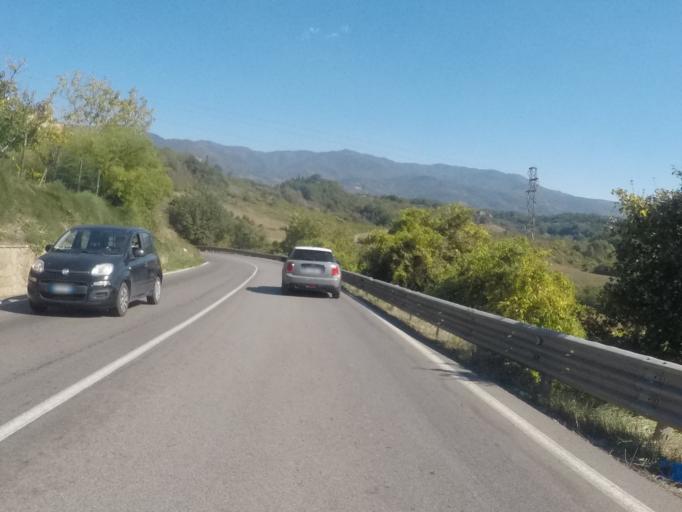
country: IT
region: Tuscany
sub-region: Province of Florence
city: Incisa in Val d'Arno
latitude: 43.6727
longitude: 11.4586
